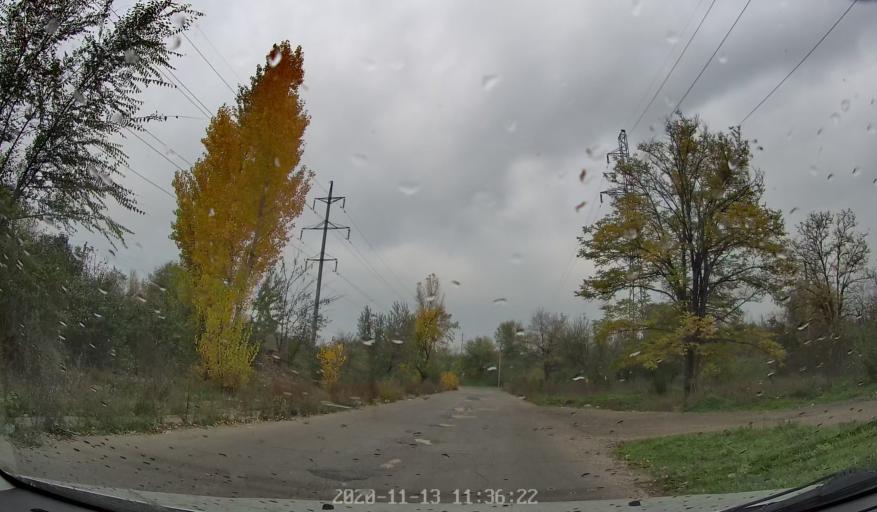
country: MD
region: Chisinau
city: Chisinau
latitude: 46.9884
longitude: 28.9158
